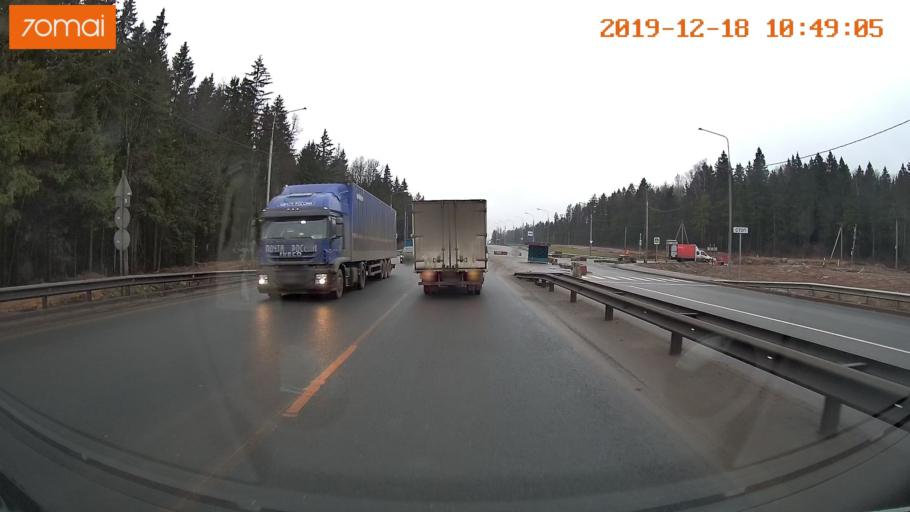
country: RU
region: Moskovskaya
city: Selyatino
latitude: 55.5011
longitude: 37.0203
